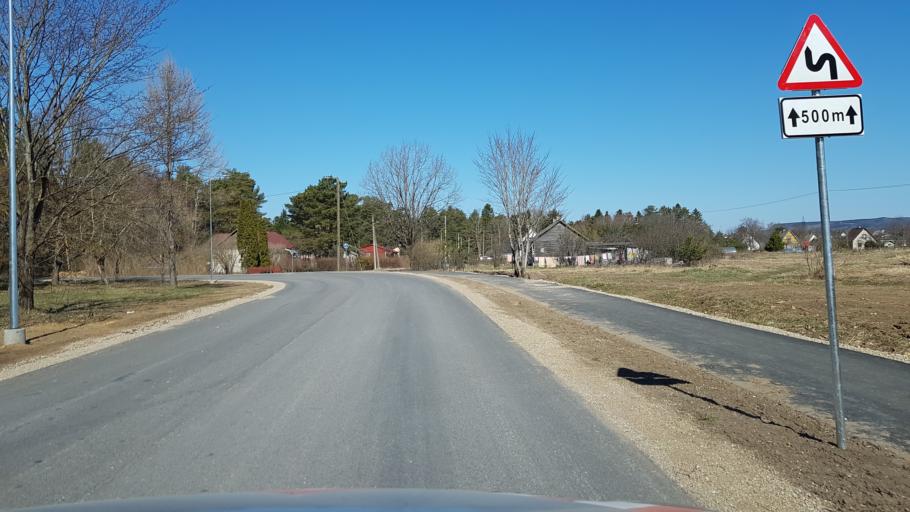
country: EE
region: Ida-Virumaa
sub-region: Kohtla-Nomme vald
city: Kohtla-Nomme
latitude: 59.3572
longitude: 27.1910
